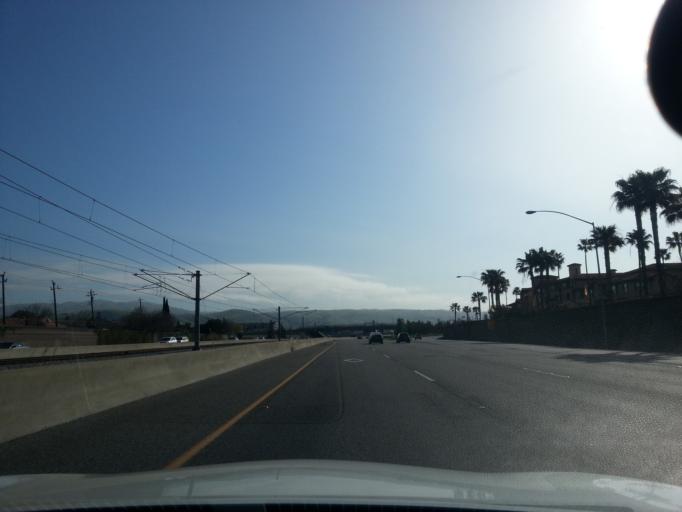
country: US
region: California
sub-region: Santa Clara County
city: Seven Trees
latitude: 37.2431
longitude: -121.8096
